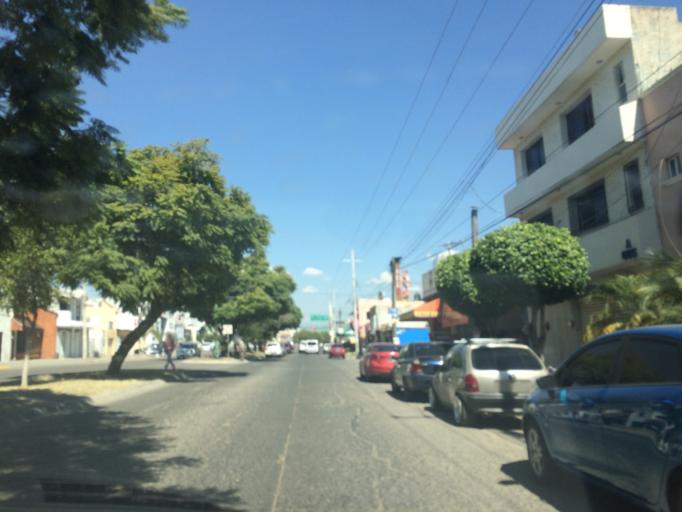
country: MX
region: Guanajuato
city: Leon
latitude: 21.0958
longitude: -101.6469
